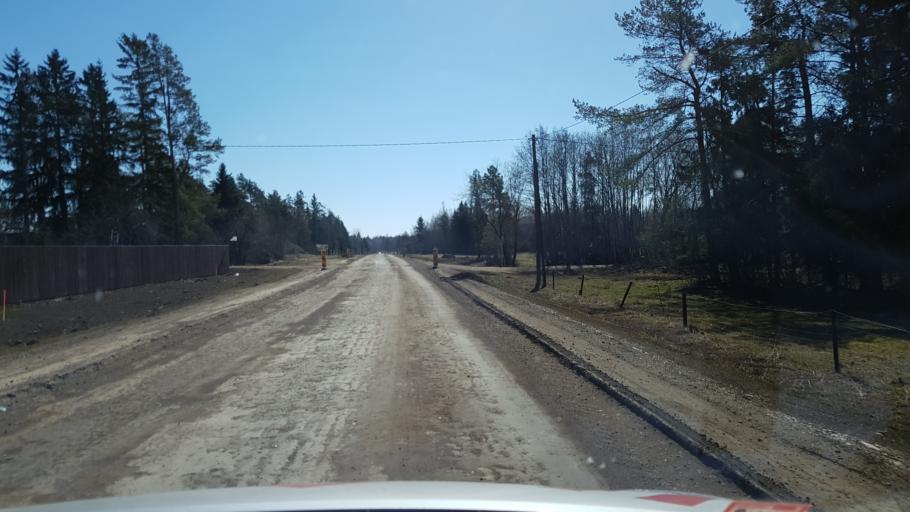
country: EE
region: Laeaene-Virumaa
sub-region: Vinni vald
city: Vinni
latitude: 59.0621
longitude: 26.6412
